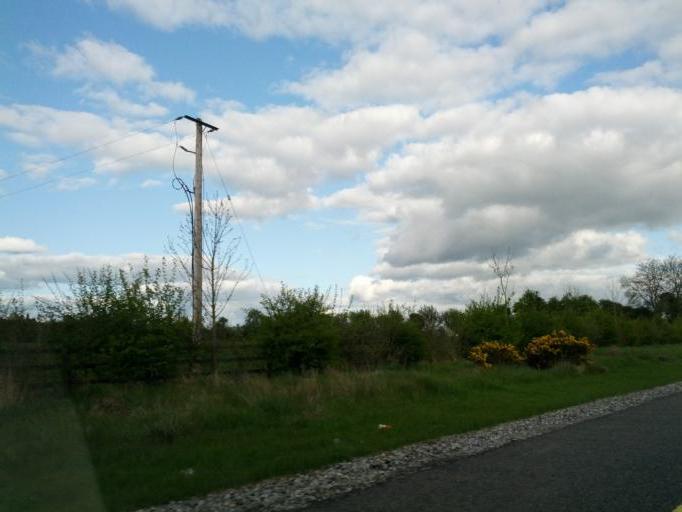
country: IE
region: Leinster
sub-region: An Iarmhi
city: Kilbeggan
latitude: 53.3782
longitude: -7.5610
